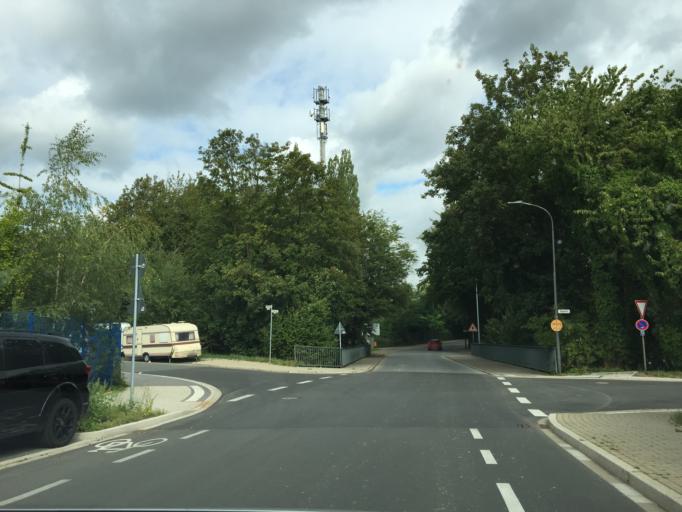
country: DE
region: North Rhine-Westphalia
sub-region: Regierungsbezirk Dusseldorf
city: Heiligenhaus
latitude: 51.3291
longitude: 6.9546
